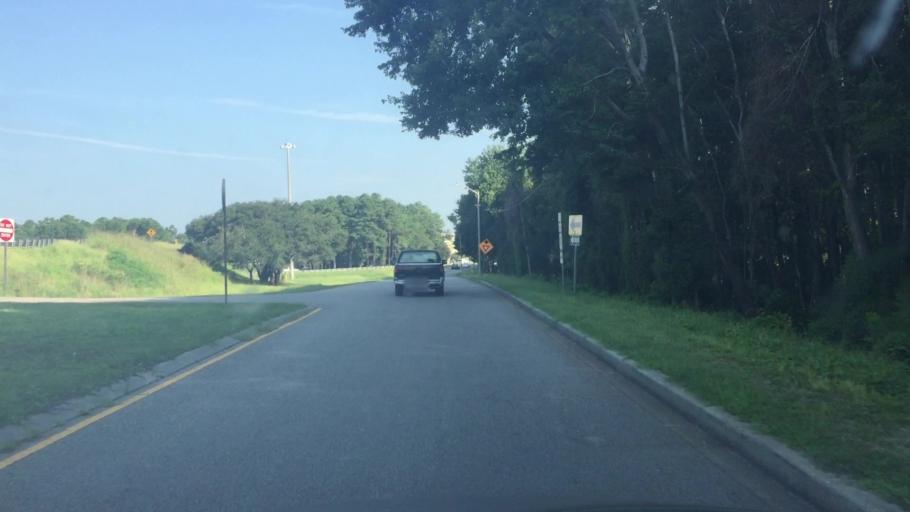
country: US
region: South Carolina
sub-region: Horry County
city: North Myrtle Beach
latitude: 33.8458
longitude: -78.6514
